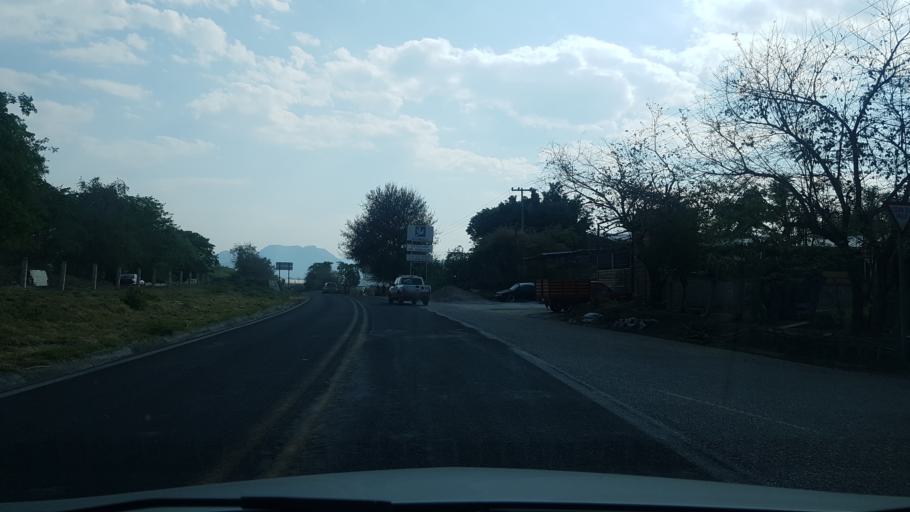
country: MX
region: Morelos
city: Puente de Ixtla
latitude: 18.6295
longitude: -99.3271
